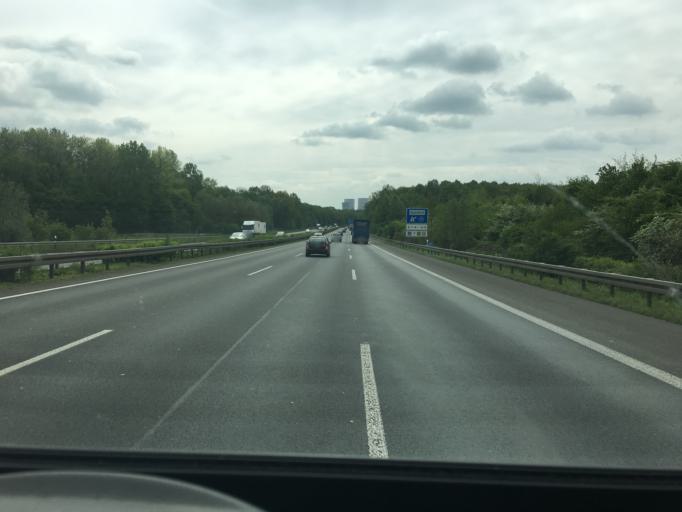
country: DE
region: North Rhine-Westphalia
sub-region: Regierungsbezirk Munster
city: Beckum
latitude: 51.7131
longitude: 7.9787
